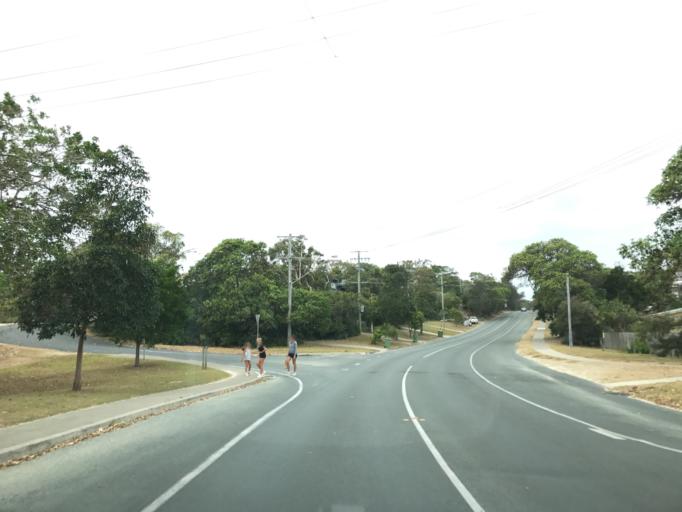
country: AU
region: Queensland
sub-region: Redland
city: Victoria Point
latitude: -27.4270
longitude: 153.5366
